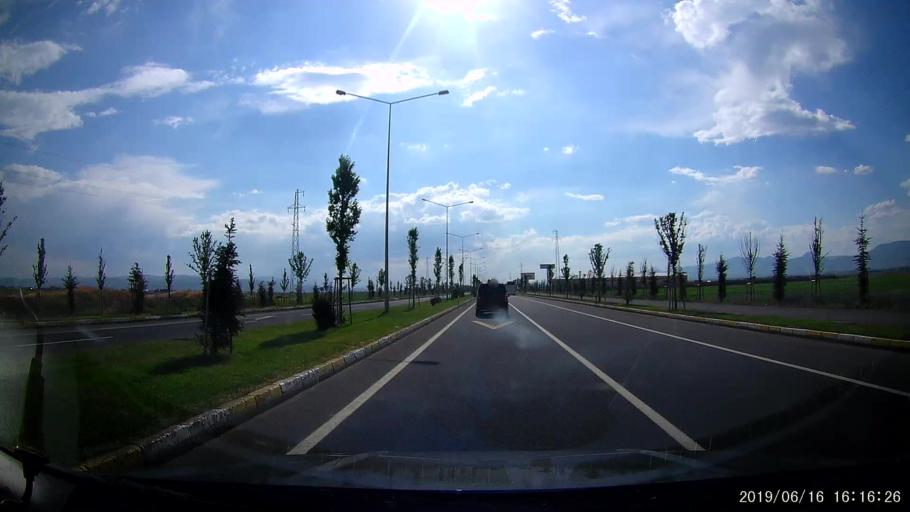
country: TR
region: Erzurum
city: Erzurum
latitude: 39.9629
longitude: 41.2049
